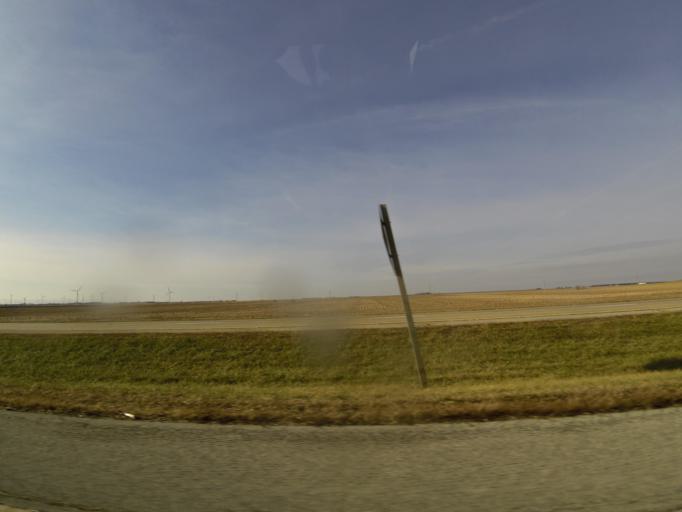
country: US
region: Illinois
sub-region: Macon County
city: Maroa
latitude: 40.0641
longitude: -88.9656
